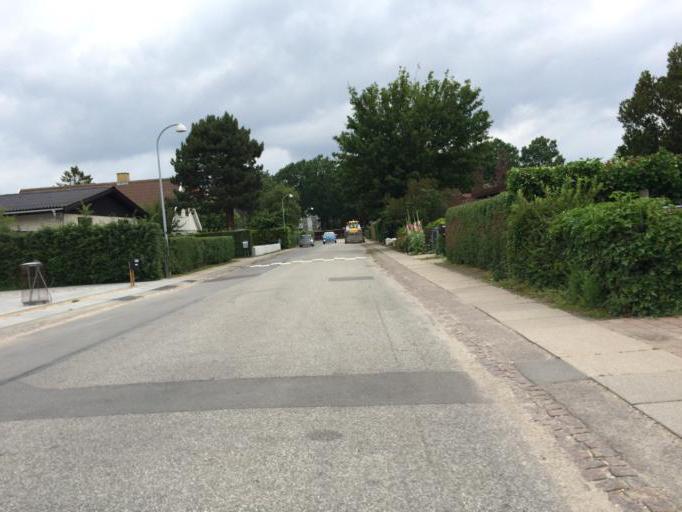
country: DK
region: Capital Region
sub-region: Hvidovre Kommune
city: Hvidovre
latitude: 55.6219
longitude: 12.4808
